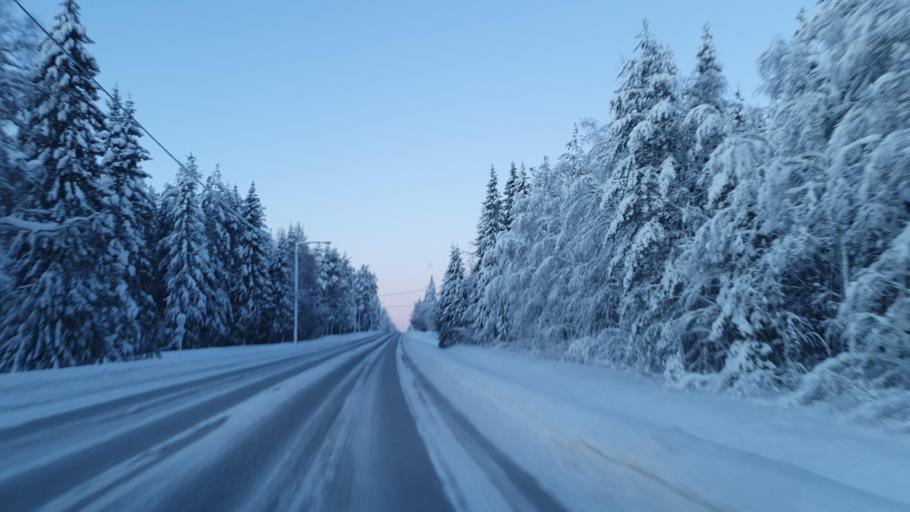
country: FI
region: Lapland
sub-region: Kemi-Tornio
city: Tornio
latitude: 66.0270
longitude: 24.0366
